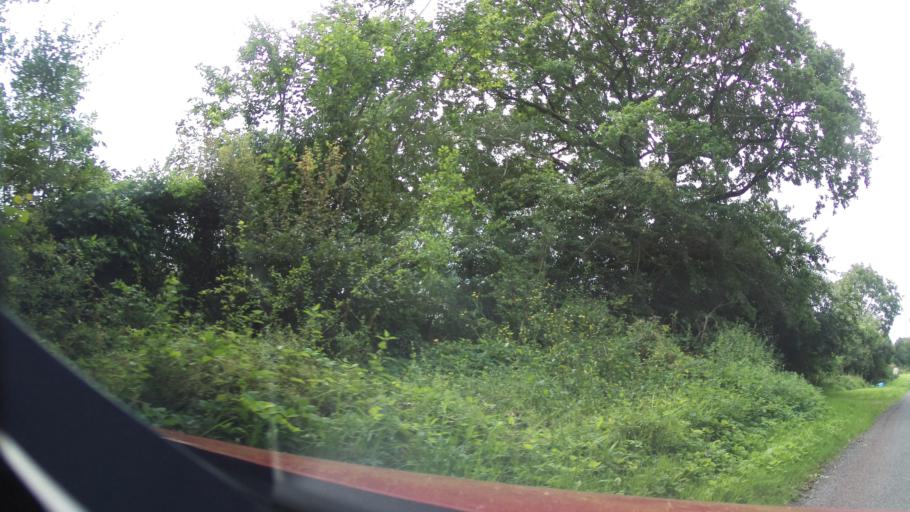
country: GB
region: England
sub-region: Somerset
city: Shepton Mallet
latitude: 51.2113
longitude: -2.5015
